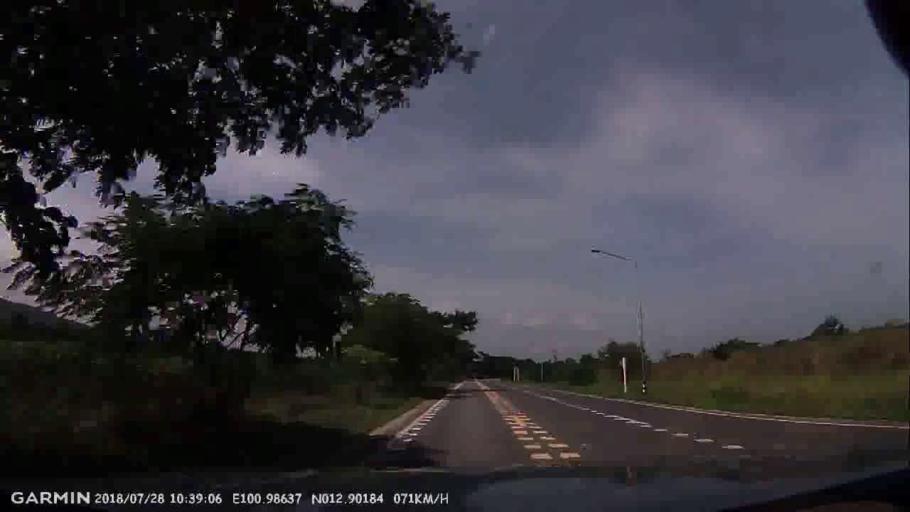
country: TH
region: Chon Buri
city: Phatthaya
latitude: 12.9017
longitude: 100.9864
